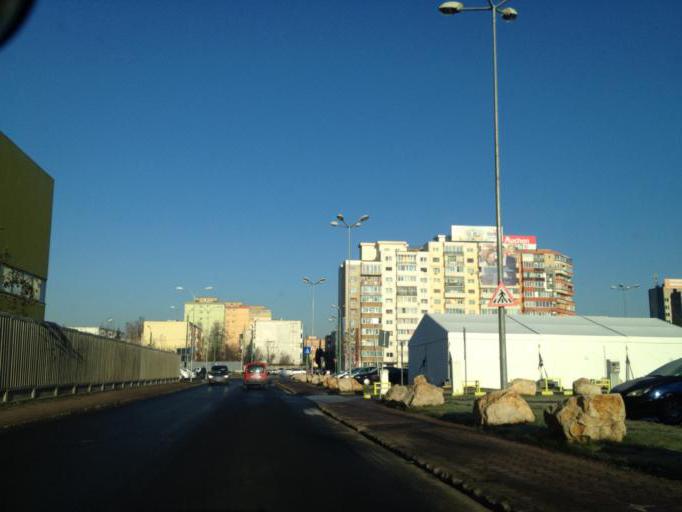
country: RO
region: Brasov
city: Brasov
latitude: 45.6326
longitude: 25.6339
